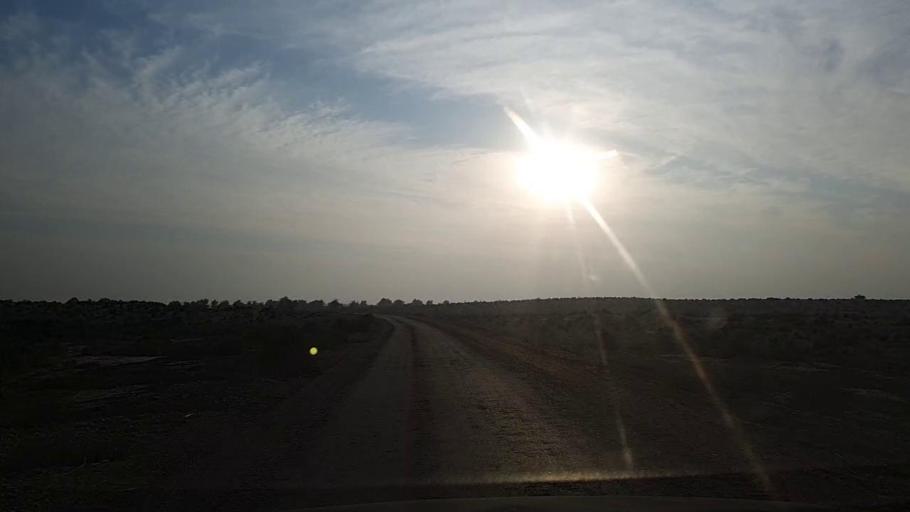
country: PK
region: Sindh
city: Jam Sahib
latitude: 26.4132
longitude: 68.5135
